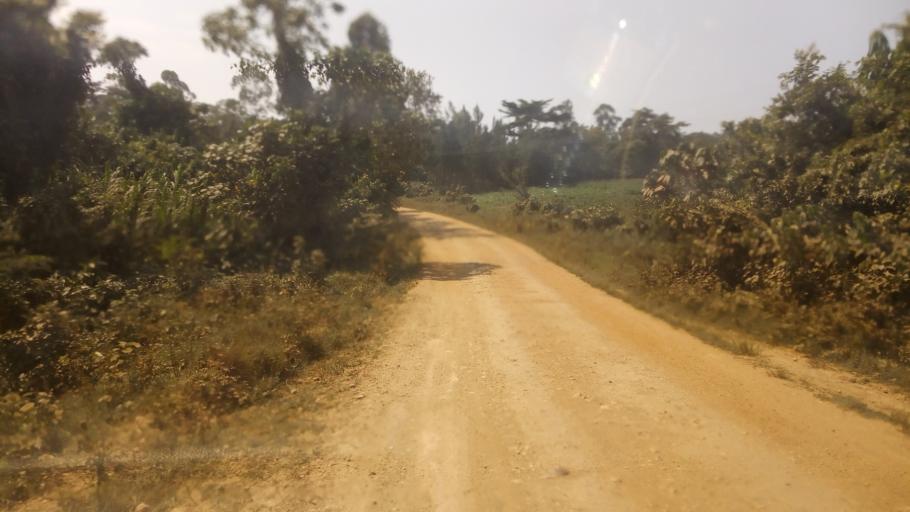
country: UG
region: Western Region
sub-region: Kanungu District
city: Ntungamo
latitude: -0.9132
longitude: 29.6231
